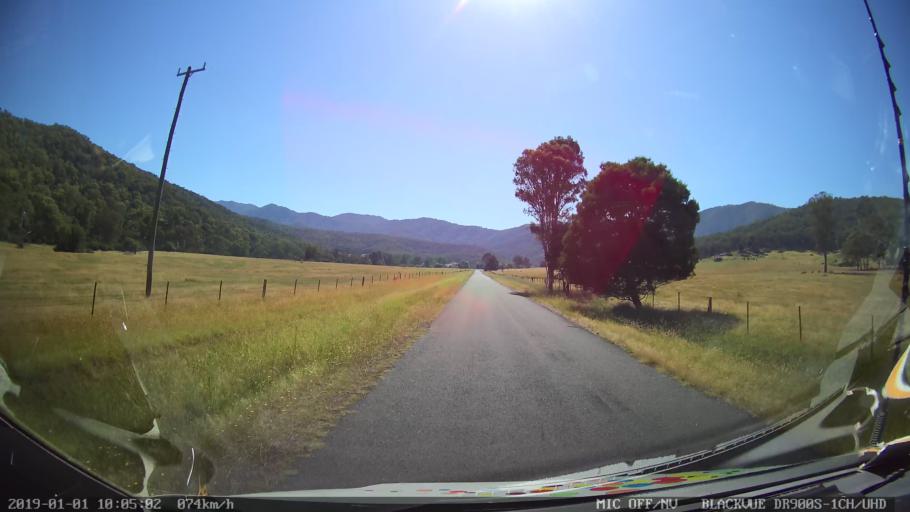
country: AU
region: New South Wales
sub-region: Snowy River
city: Jindabyne
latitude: -36.1744
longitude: 148.1305
